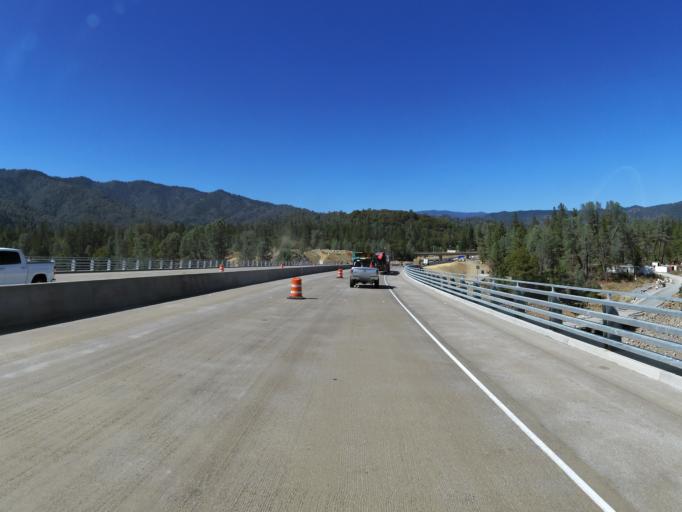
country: US
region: California
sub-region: Shasta County
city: Central Valley (historical)
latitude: 40.8818
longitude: -122.3814
